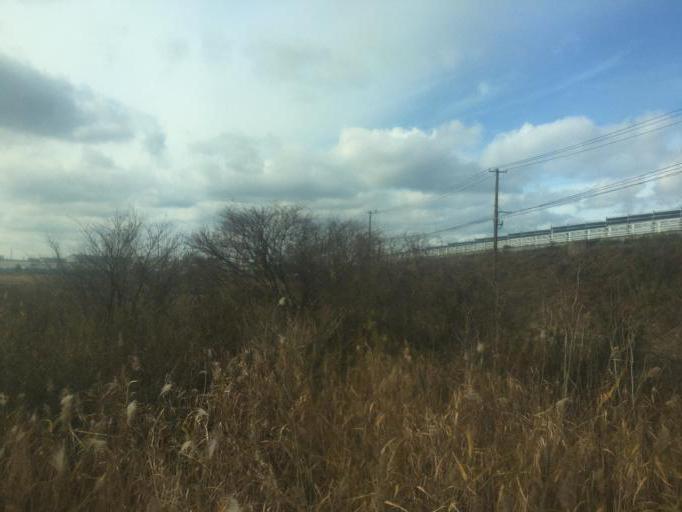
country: JP
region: Akita
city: Noshiromachi
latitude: 40.1844
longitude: 140.0591
